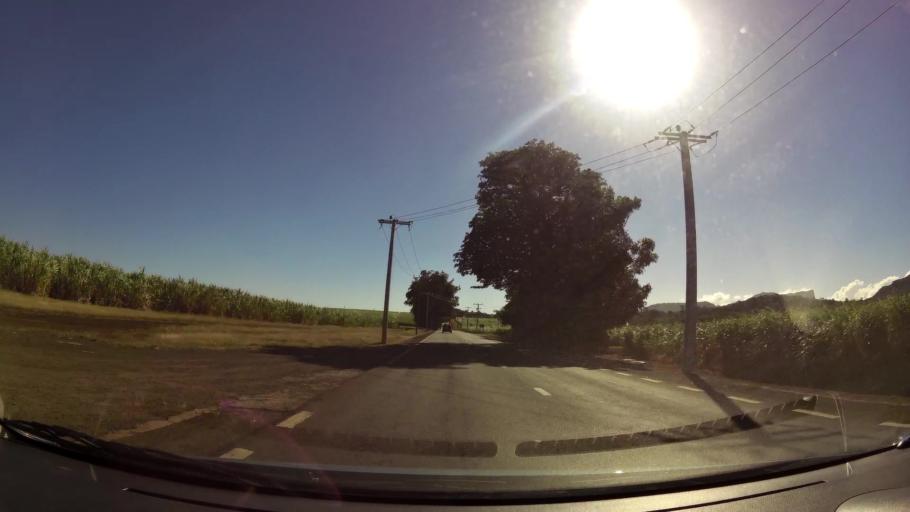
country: MU
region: Black River
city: Cascavelle
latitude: -20.2979
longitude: 57.4009
